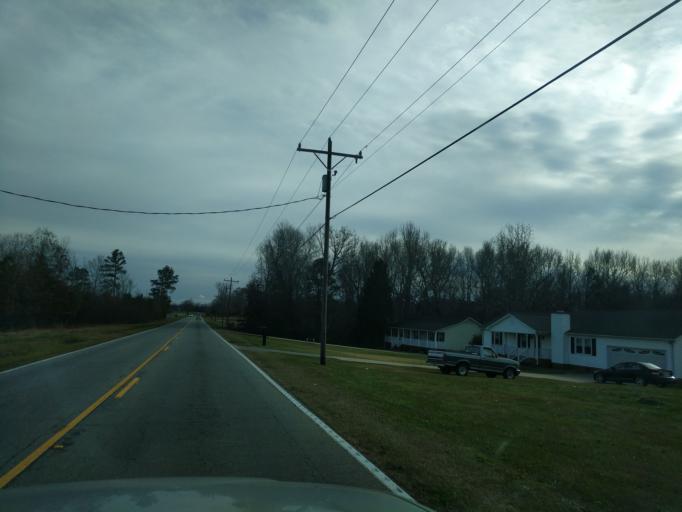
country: US
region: South Carolina
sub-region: Anderson County
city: Piedmont
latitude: 34.7157
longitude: -82.5631
